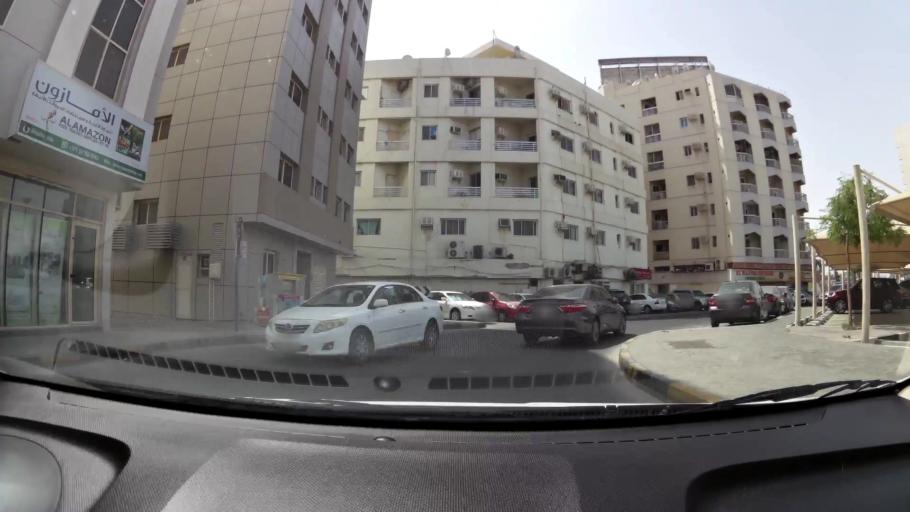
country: AE
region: Ash Shariqah
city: Sharjah
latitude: 25.3532
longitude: 55.3838
